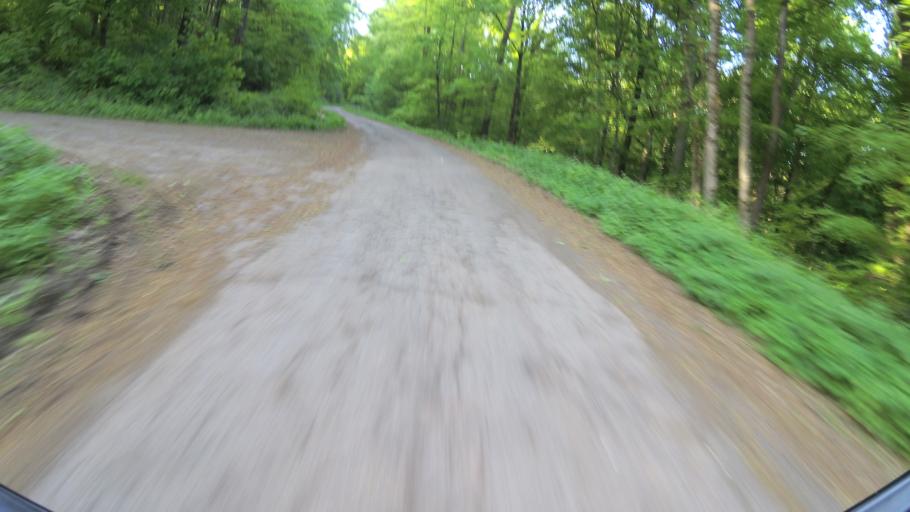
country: DE
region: Saarland
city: Illingen
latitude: 49.4108
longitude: 7.0418
